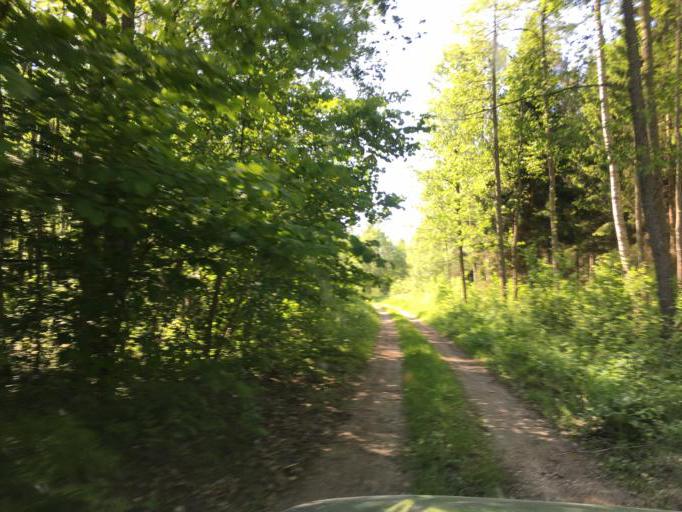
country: LV
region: Ventspils
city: Ventspils
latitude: 57.4776
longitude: 21.7630
